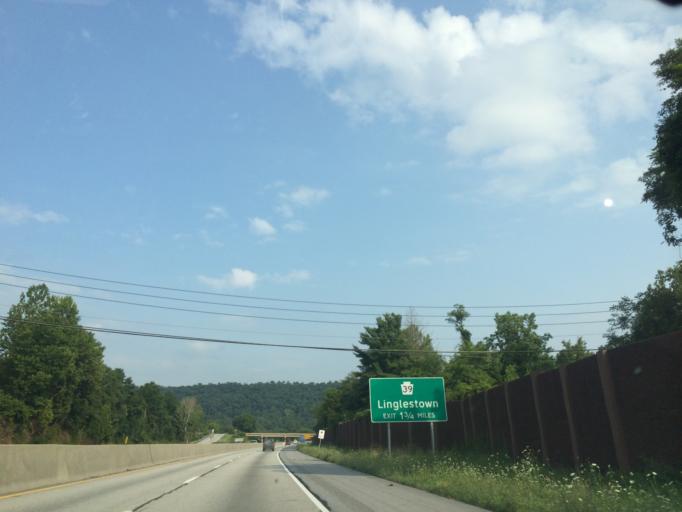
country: US
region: Pennsylvania
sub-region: Perry County
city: Marysville
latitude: 40.3503
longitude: -76.9132
